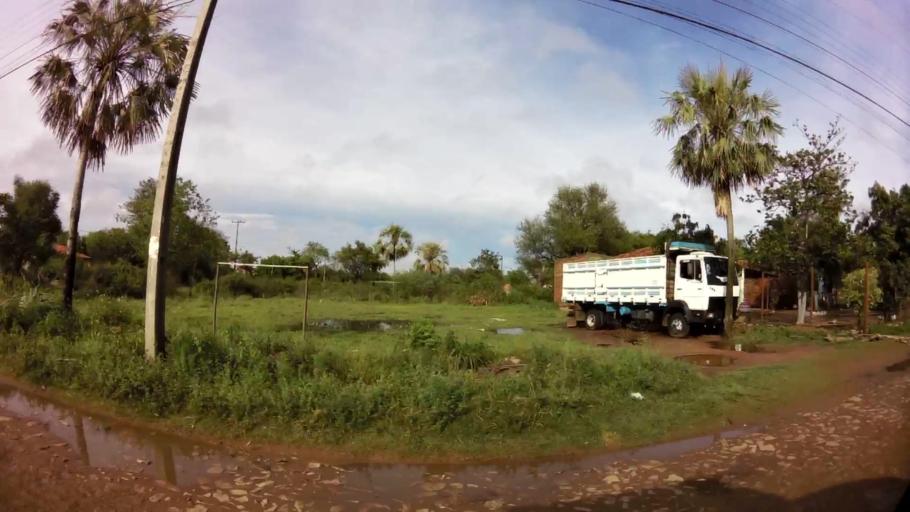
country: PY
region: Central
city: Limpio
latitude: -25.1857
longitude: -57.4877
